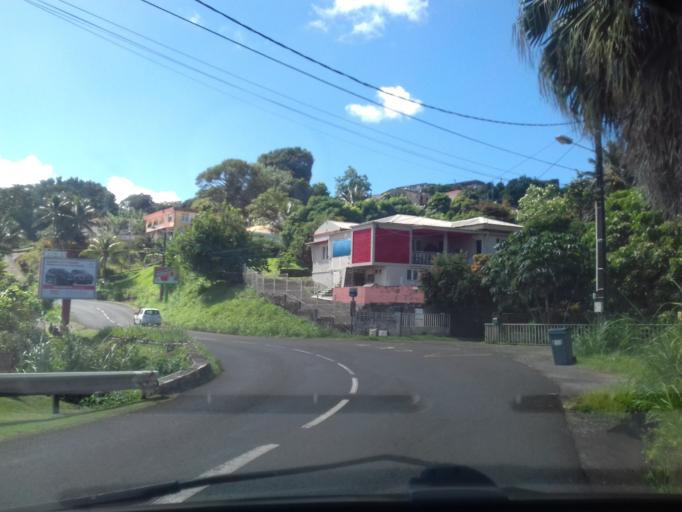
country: MQ
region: Martinique
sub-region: Martinique
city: Saint-Joseph
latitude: 14.6458
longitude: -61.0531
